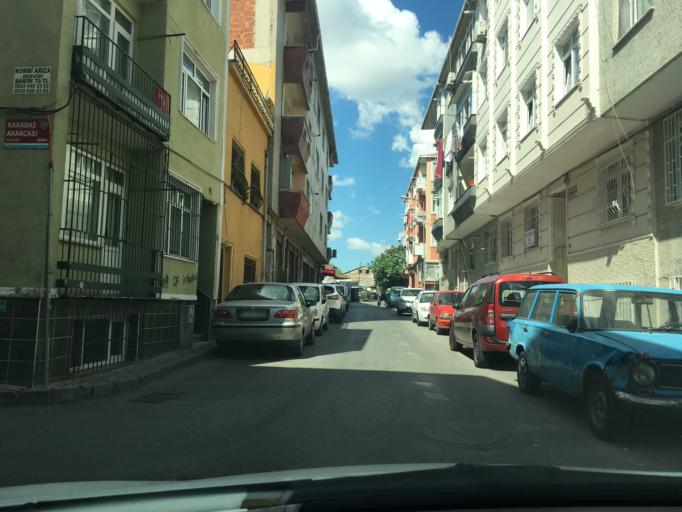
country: TR
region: Istanbul
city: Istanbul
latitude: 41.0118
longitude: 28.9243
